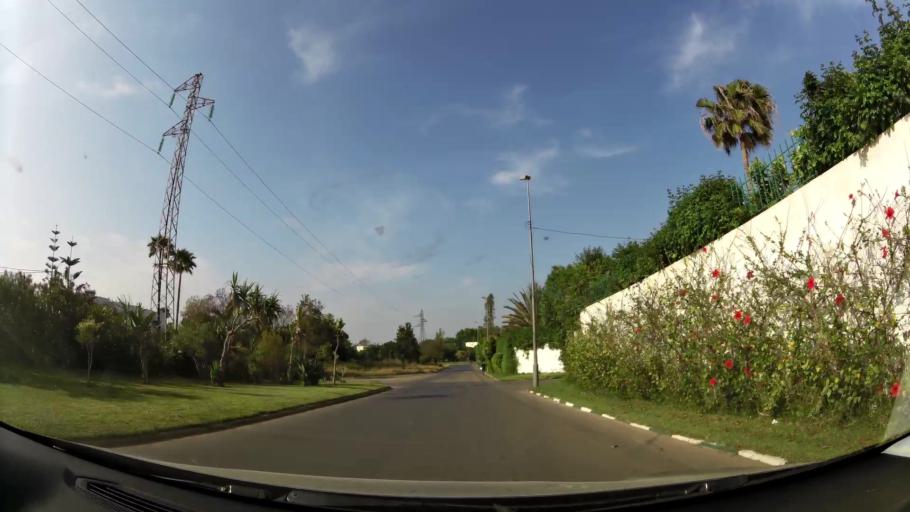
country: MA
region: Rabat-Sale-Zemmour-Zaer
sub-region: Rabat
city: Rabat
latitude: 33.9399
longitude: -6.8072
